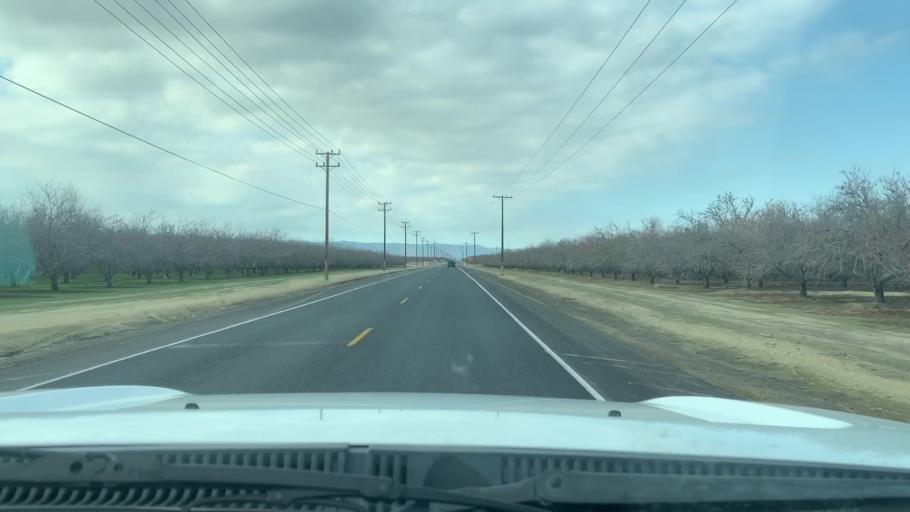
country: US
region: California
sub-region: Kern County
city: Lost Hills
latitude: 35.4992
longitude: -119.6847
